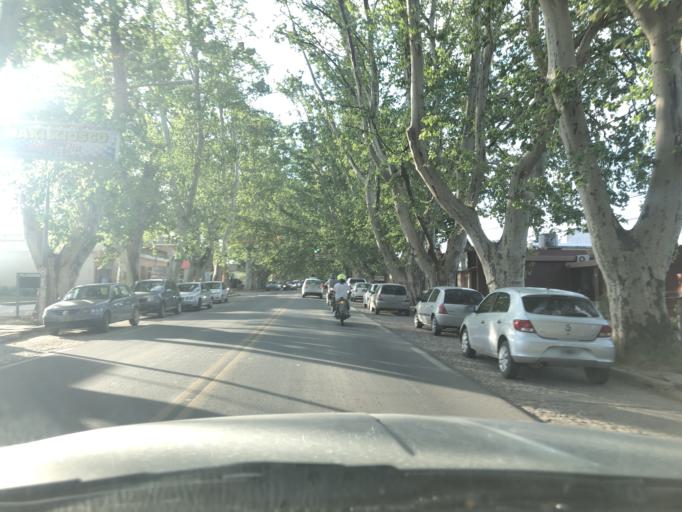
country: AR
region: Cordoba
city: Jesus Maria
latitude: -31.0062
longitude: -64.0794
